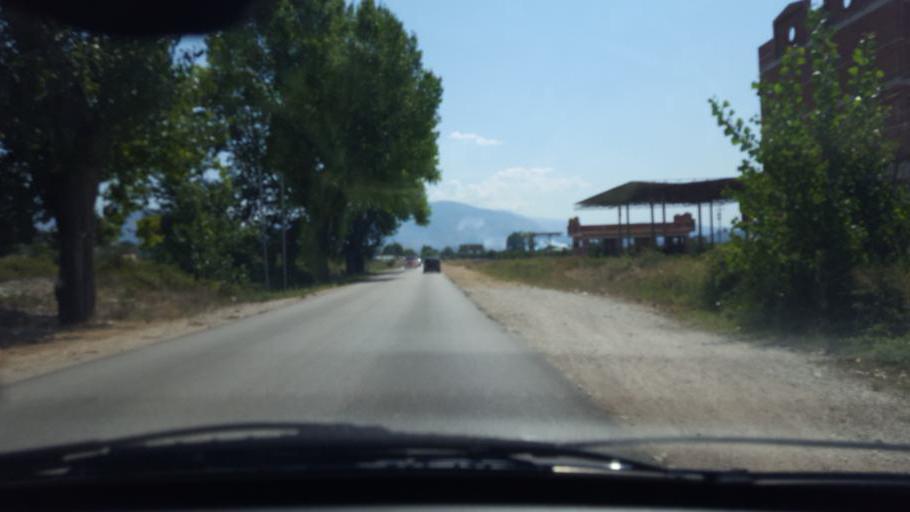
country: AL
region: Vlore
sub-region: Rrethi i Delvines
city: Finiq
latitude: 39.8793
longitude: 20.0441
